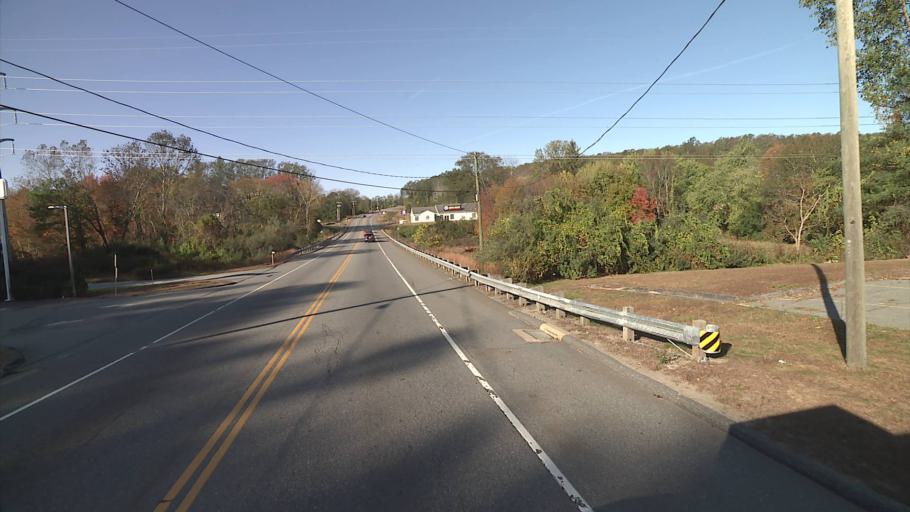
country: US
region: Connecticut
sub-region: Windham County
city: East Brooklyn
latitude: 41.7967
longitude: -71.9156
